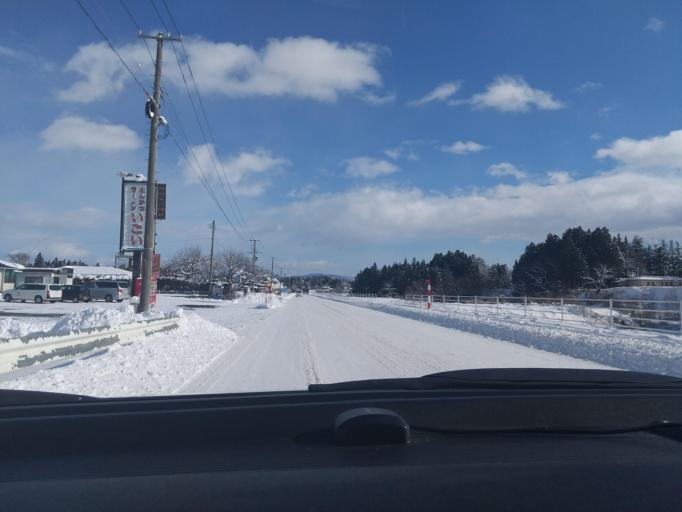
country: JP
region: Iwate
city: Hanamaki
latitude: 39.4252
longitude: 141.0783
